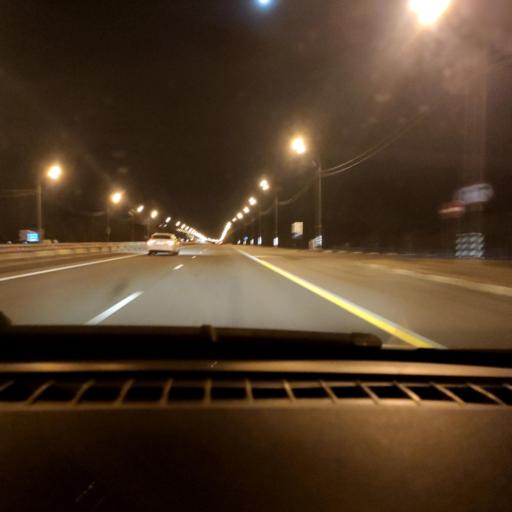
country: RU
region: Lipetsk
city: Khlevnoye
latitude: 52.2308
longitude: 39.0908
